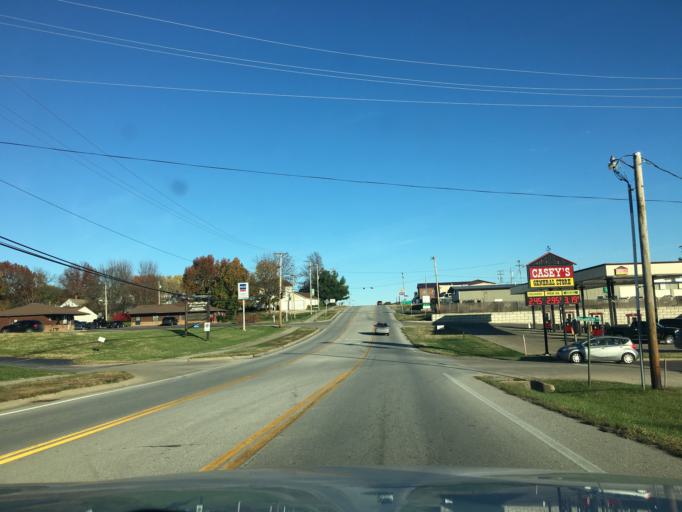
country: US
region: Missouri
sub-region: Franklin County
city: New Haven
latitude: 38.6007
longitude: -91.2233
